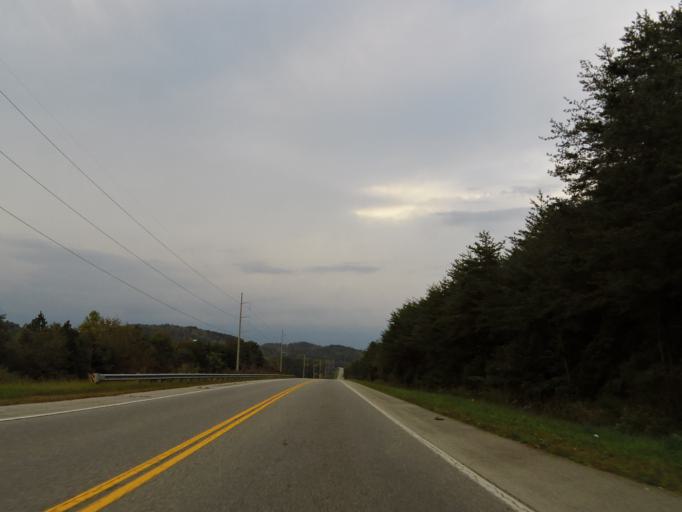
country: US
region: Tennessee
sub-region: Monroe County
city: Vonore
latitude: 35.6192
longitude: -84.2743
